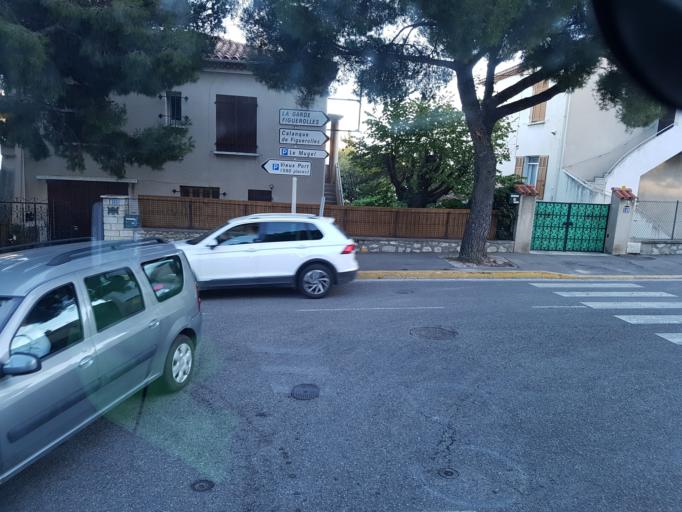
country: FR
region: Provence-Alpes-Cote d'Azur
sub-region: Departement des Bouches-du-Rhone
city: La Ciotat
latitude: 43.1706
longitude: 5.6016
